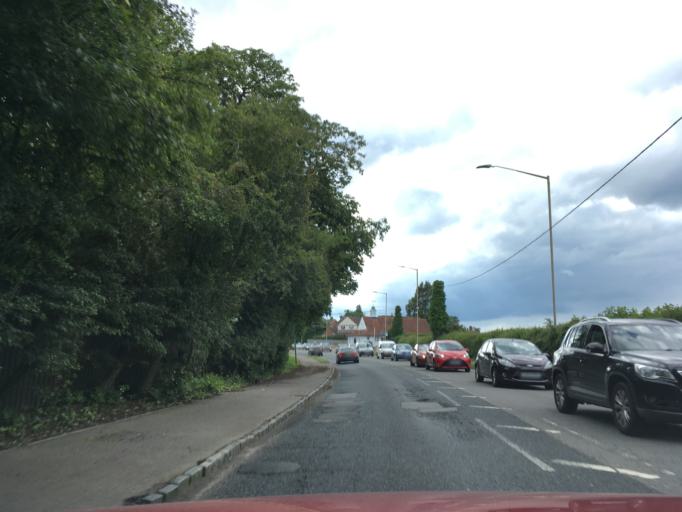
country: GB
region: England
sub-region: Buckinghamshire
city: Stone
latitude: 51.8045
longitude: -0.8617
